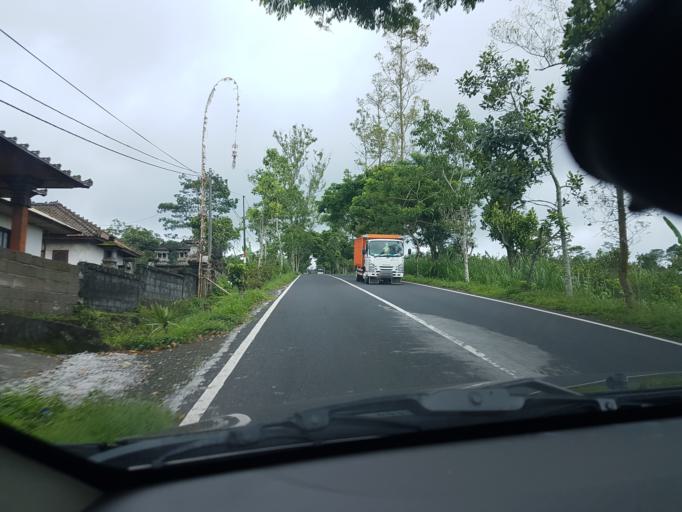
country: ID
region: Bali
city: Banjar Kedisan
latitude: -8.2899
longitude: 115.3608
